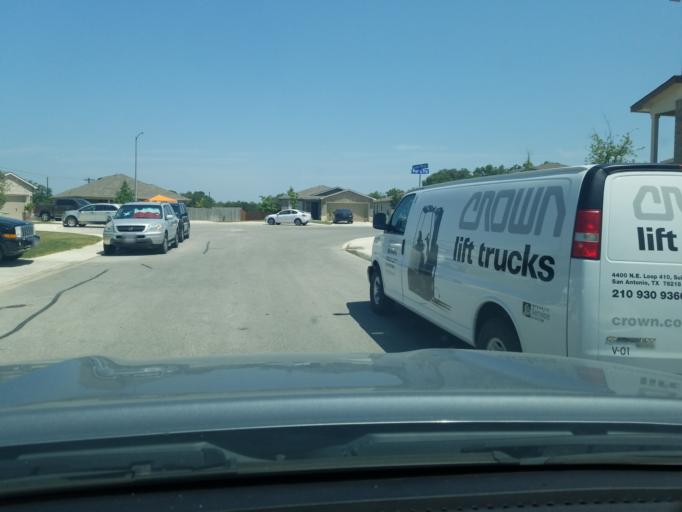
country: US
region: Texas
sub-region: Bexar County
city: Timberwood Park
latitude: 29.7076
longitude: -98.4831
